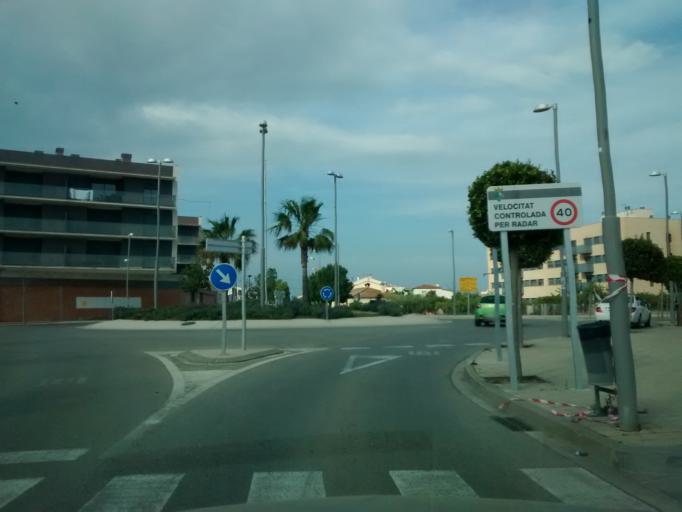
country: ES
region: Catalonia
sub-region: Provincia de Tarragona
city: Deltebre
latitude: 40.7153
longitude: 0.7186
